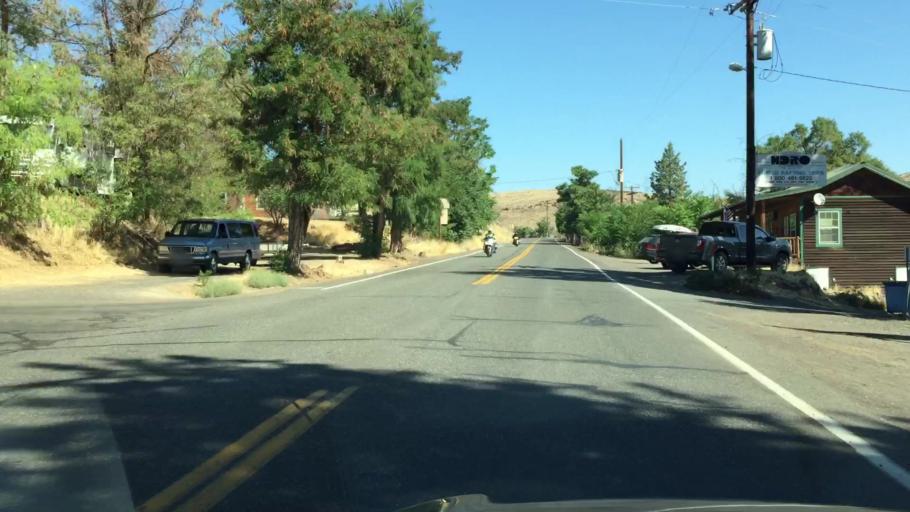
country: US
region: Oregon
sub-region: Wasco County
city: The Dalles
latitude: 45.1744
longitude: -121.0763
